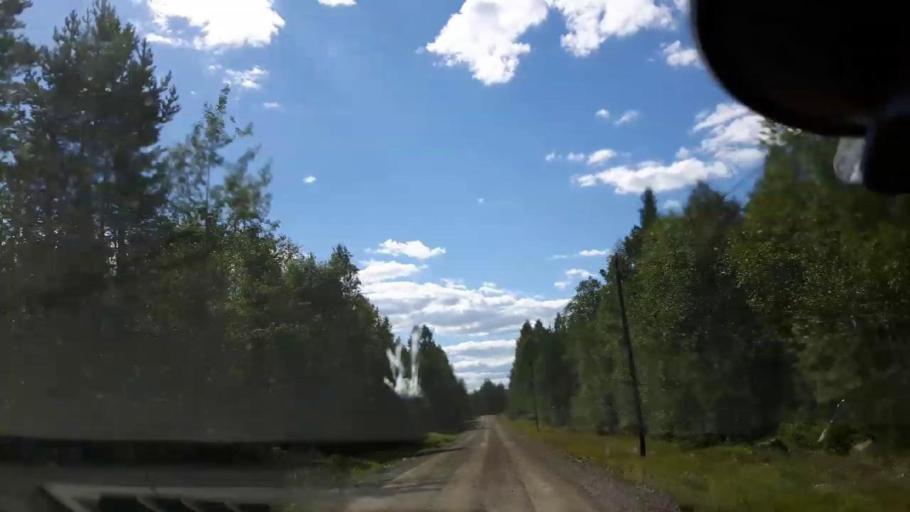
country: SE
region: Vaesternorrland
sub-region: Ange Kommun
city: Fransta
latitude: 62.7894
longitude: 16.1434
